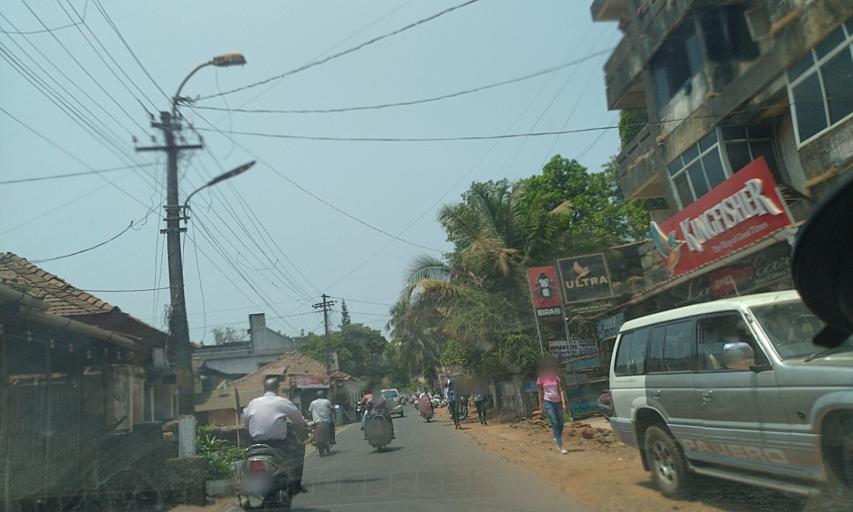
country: IN
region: Goa
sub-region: North Goa
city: Mapuca
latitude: 15.5928
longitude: 73.8058
